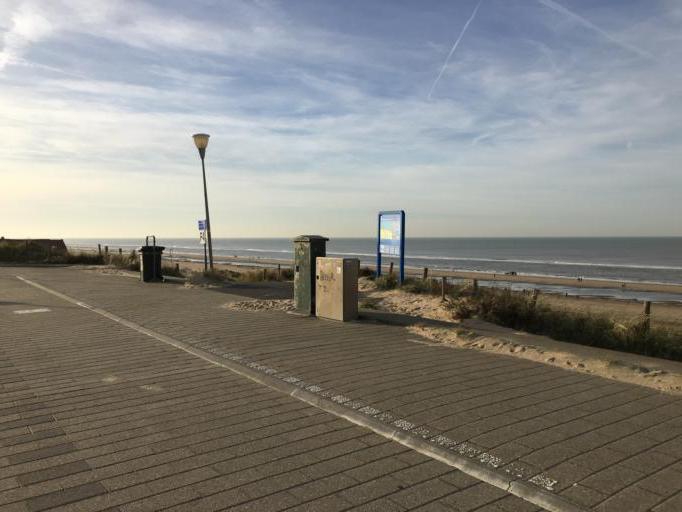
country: NL
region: North Holland
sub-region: Gemeente Zandvoort
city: Zandvoort
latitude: 52.3939
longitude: 4.5388
